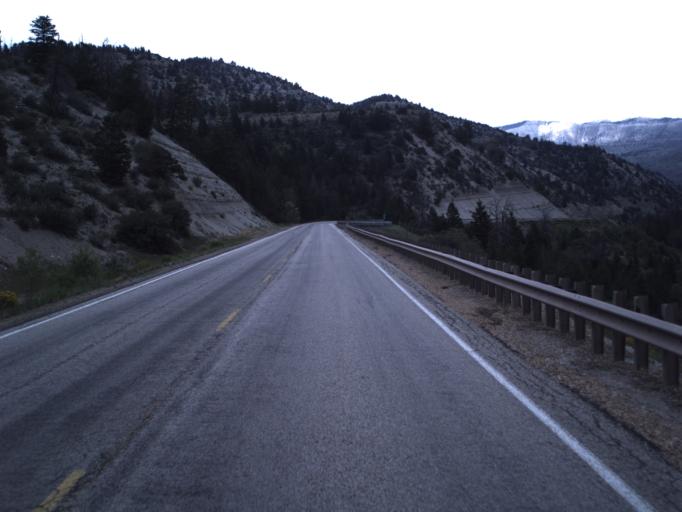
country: US
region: Utah
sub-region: Carbon County
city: Helper
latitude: 39.8998
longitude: -110.7457
